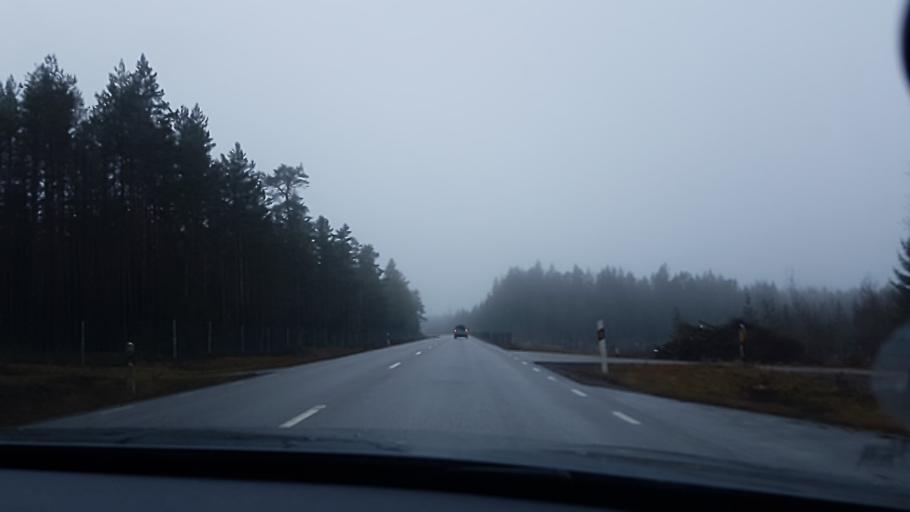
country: SE
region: Vaestra Goetaland
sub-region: Gullspangs Kommun
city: Gullspang
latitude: 58.9193
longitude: 14.0295
